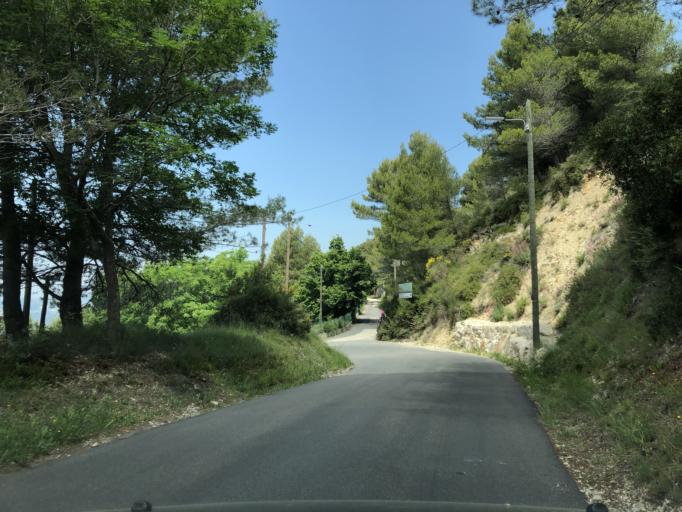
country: FR
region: Provence-Alpes-Cote d'Azur
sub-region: Departement des Alpes-Maritimes
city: Eze
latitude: 43.7349
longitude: 7.3462
